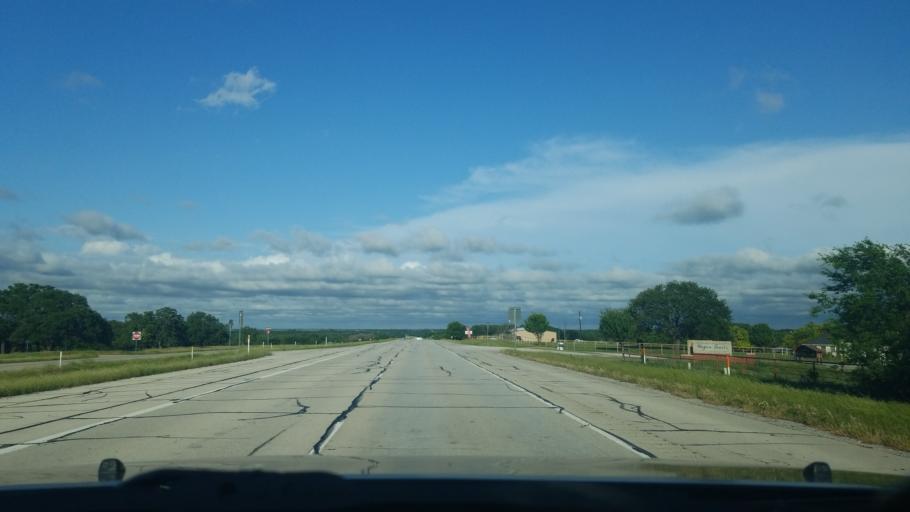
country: US
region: Texas
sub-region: Wise County
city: Decatur
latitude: 33.2450
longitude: -97.4793
